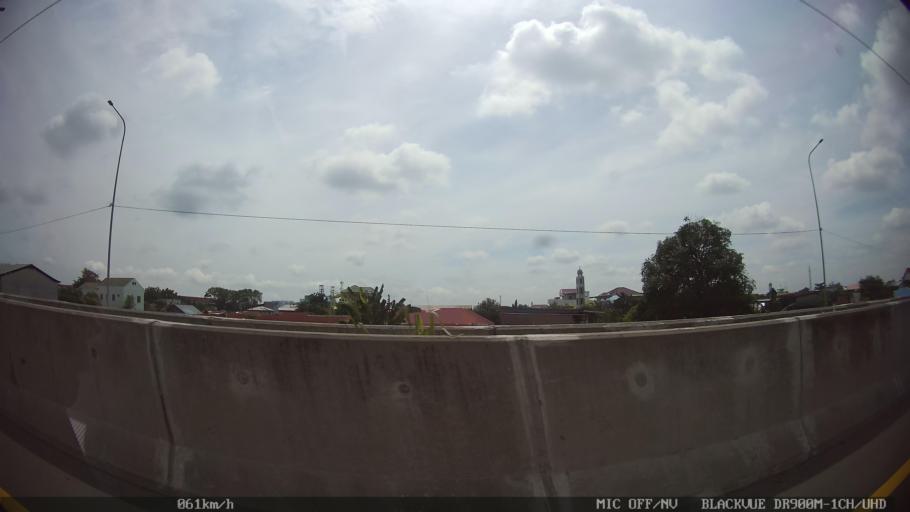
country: ID
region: North Sumatra
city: Medan
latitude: 3.6536
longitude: 98.6827
